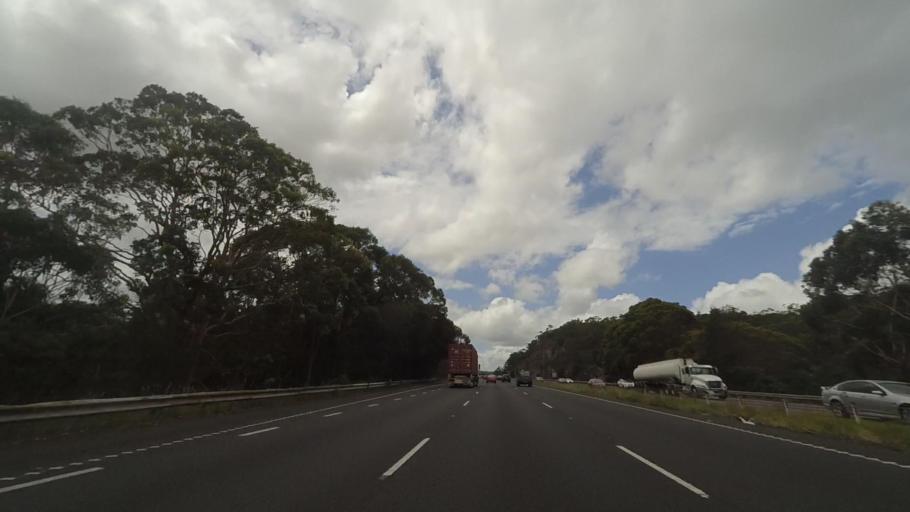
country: AU
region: New South Wales
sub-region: Gosford Shire
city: Point Clare
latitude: -33.4337
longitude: 151.2221
